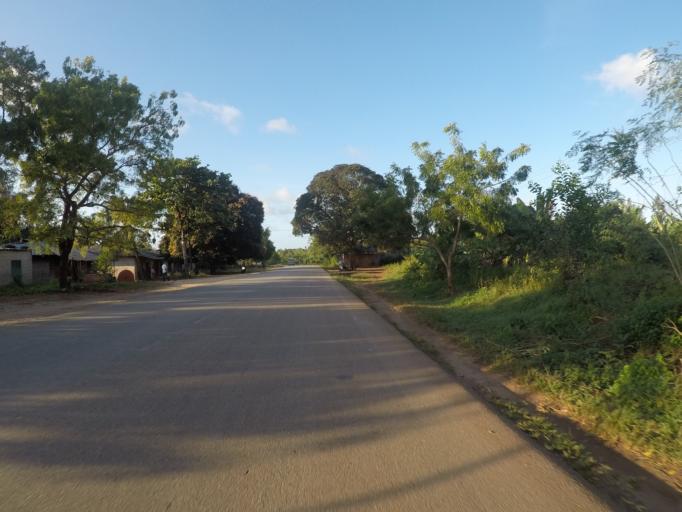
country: TZ
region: Zanzibar North
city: Kijini
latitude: -5.8122
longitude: 39.2937
